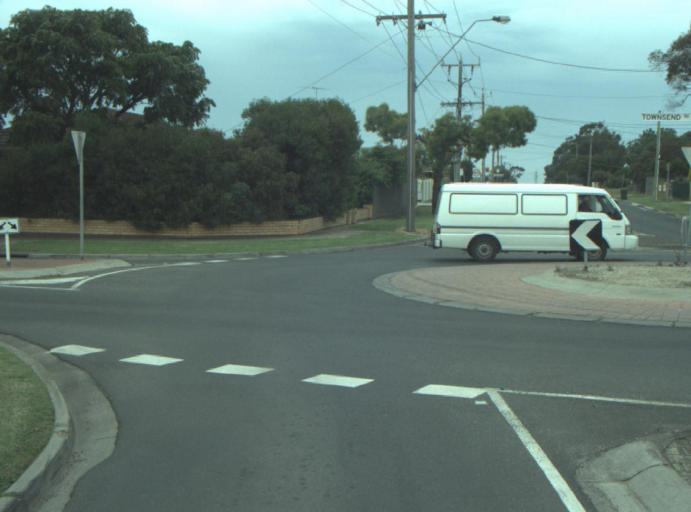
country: AU
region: Victoria
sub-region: Greater Geelong
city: Breakwater
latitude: -38.1823
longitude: 144.4009
